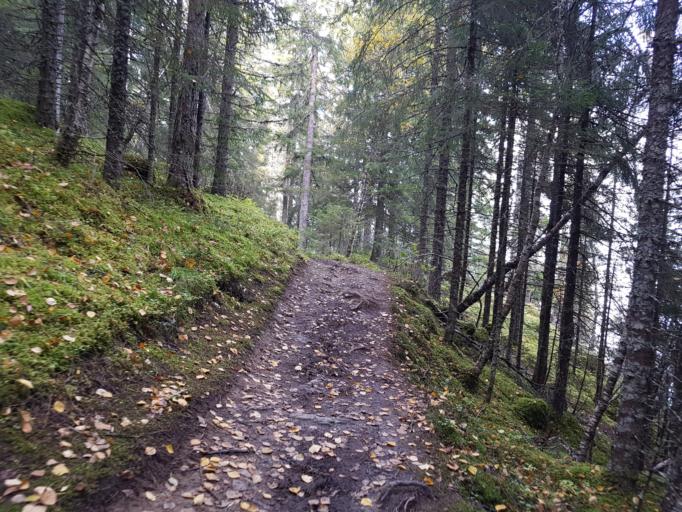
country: NO
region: Sor-Trondelag
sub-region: Trondheim
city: Trondheim
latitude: 63.4493
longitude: 10.2694
